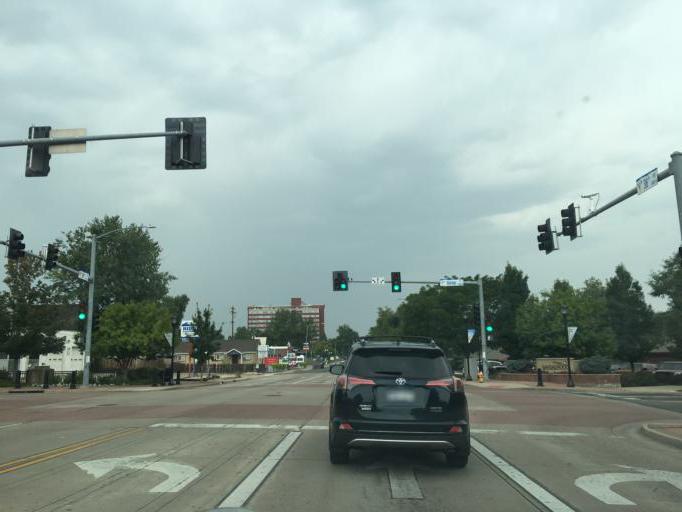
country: US
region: Colorado
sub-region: Jefferson County
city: Wheat Ridge
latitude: 39.7694
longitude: -105.0623
